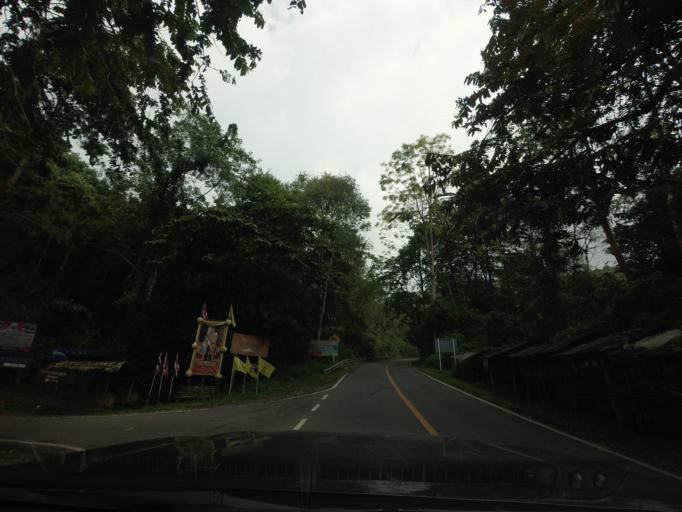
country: TH
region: Nan
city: Bo Kluea
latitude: 19.2064
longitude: 101.0706
